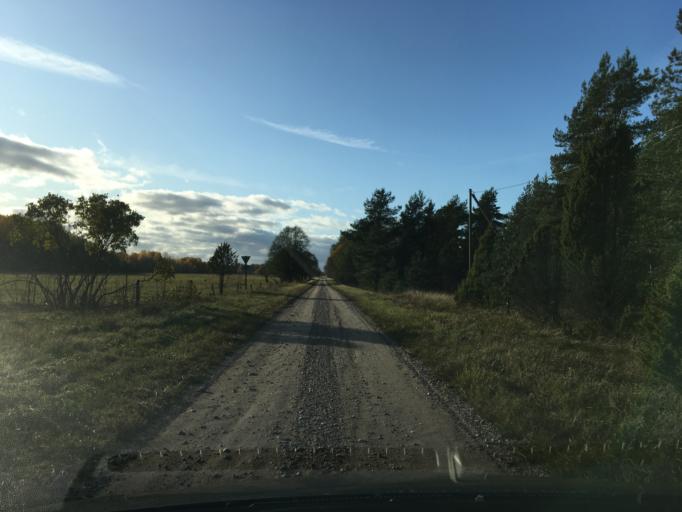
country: EE
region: Laeaene
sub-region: Lihula vald
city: Lihula
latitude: 58.5635
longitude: 23.8176
